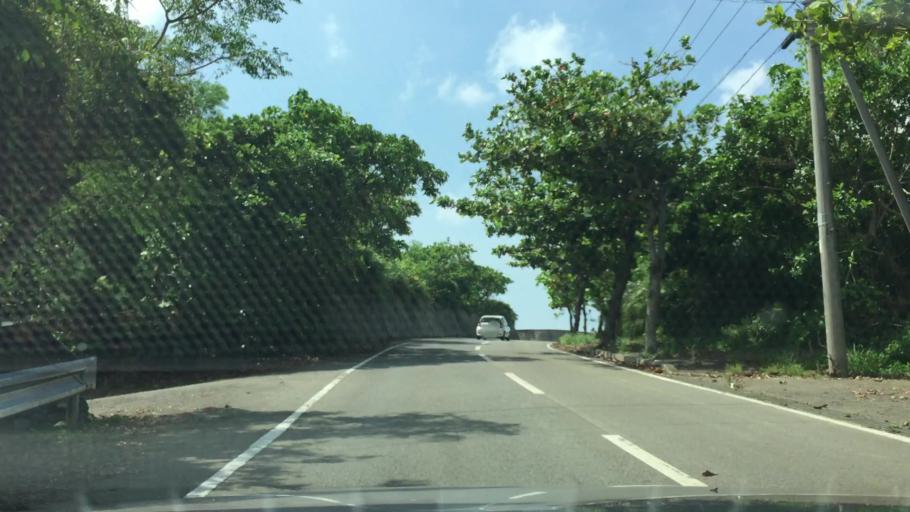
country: JP
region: Okinawa
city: Ishigaki
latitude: 24.4697
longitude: 124.2249
